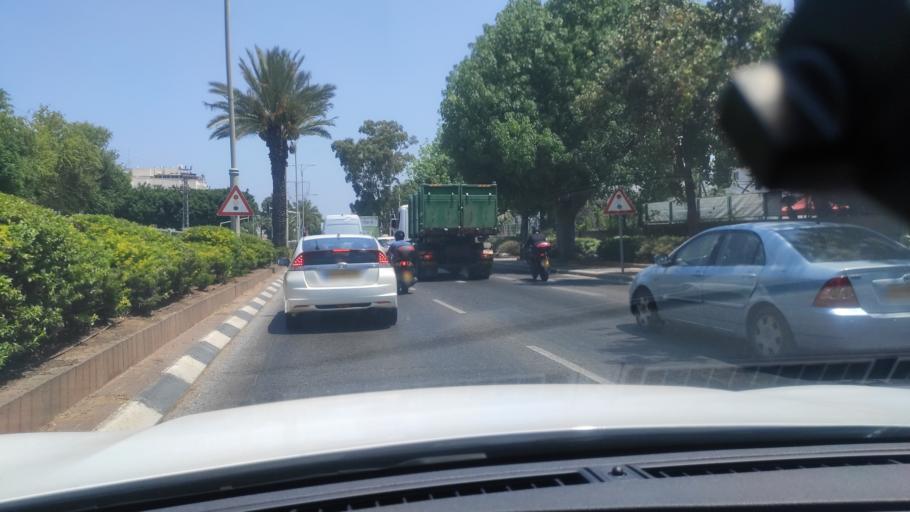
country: IL
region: Central District
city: Petah Tiqwa
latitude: 32.0899
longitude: 34.9018
